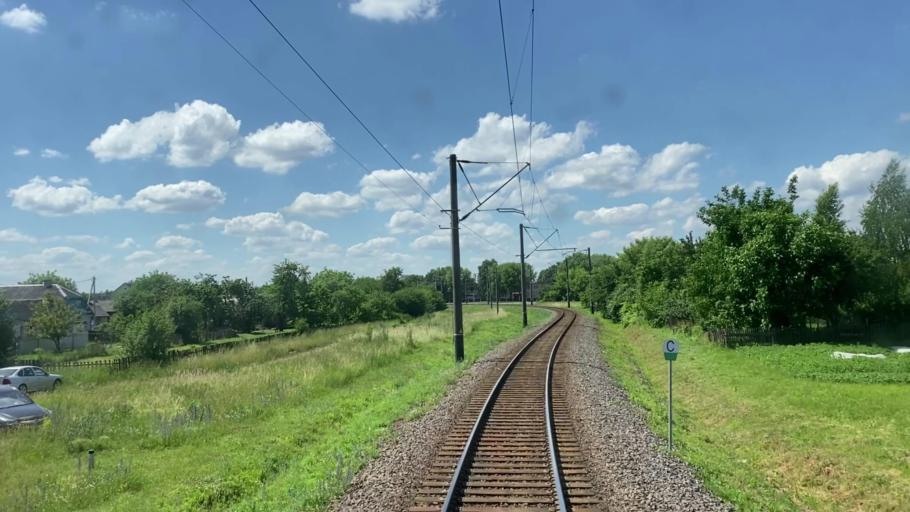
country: BY
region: Brest
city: Baranovichi
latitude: 53.1425
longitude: 26.0335
